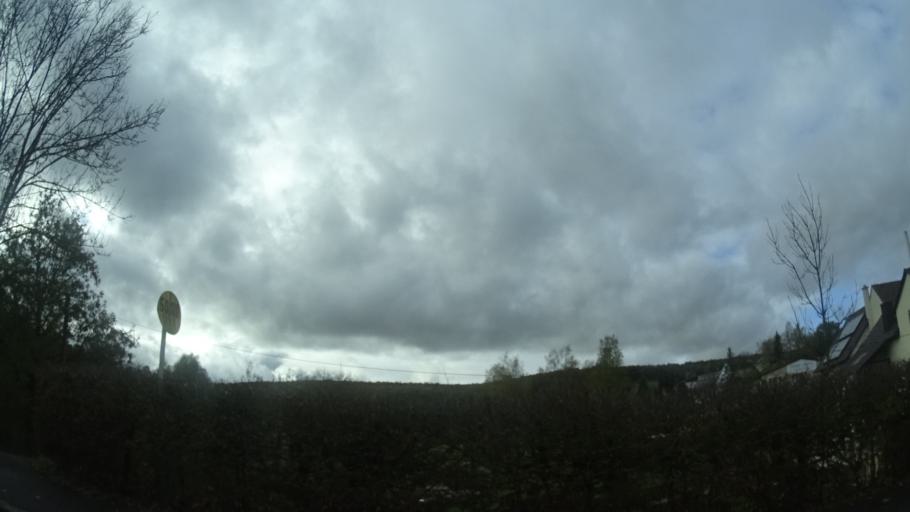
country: DE
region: Bavaria
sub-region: Regierungsbezirk Unterfranken
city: Aubstadt
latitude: 50.3566
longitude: 10.4234
